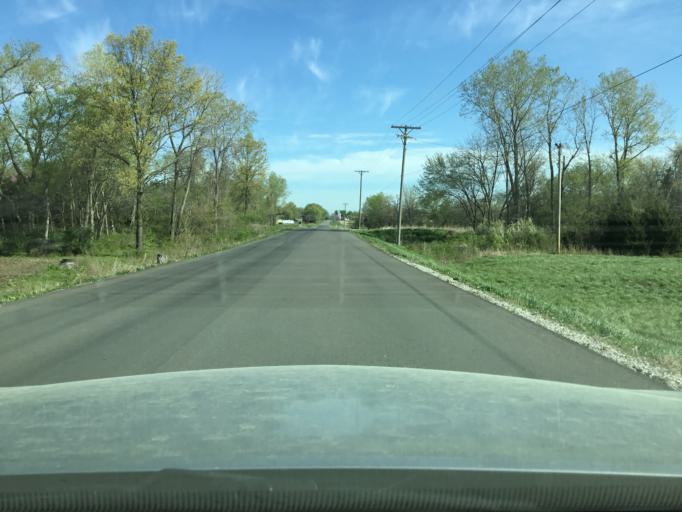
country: US
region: Kansas
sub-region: Neosho County
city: Chanute
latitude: 37.6567
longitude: -95.4435
